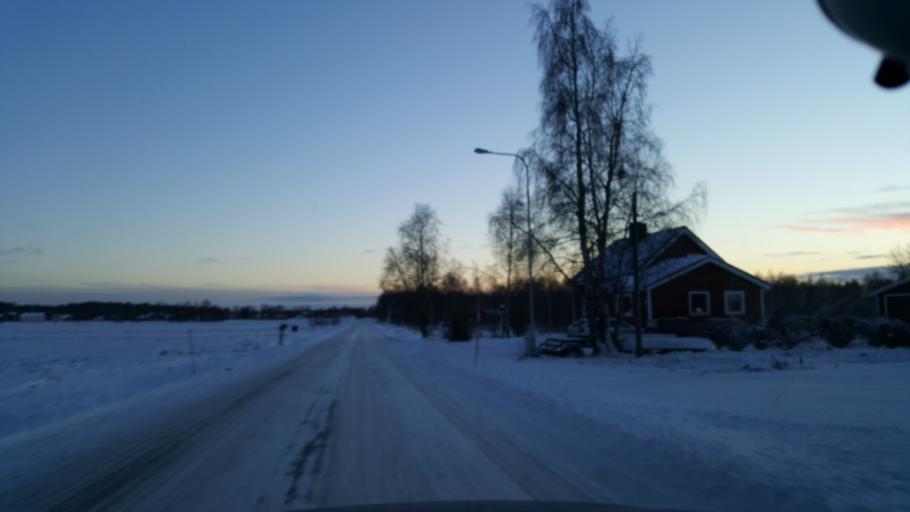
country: SE
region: Norrbotten
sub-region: Lulea Kommun
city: Sodra Sunderbyn
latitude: 65.5402
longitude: 21.9025
